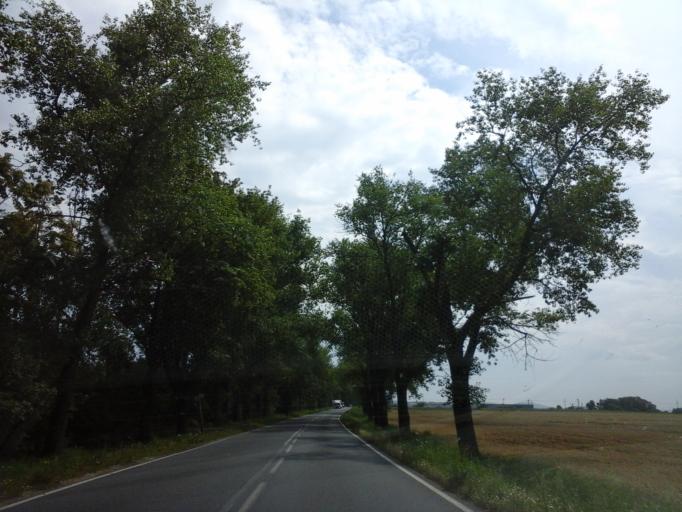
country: PL
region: Lower Silesian Voivodeship
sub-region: Powiat strzelinski
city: Strzelin
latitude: 50.7983
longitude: 17.0636
